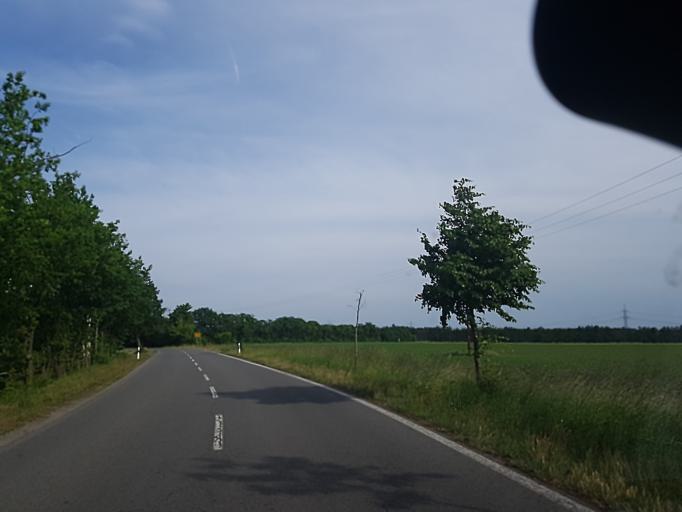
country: DE
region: Saxony-Anhalt
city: Jessen
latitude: 51.8338
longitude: 12.9367
